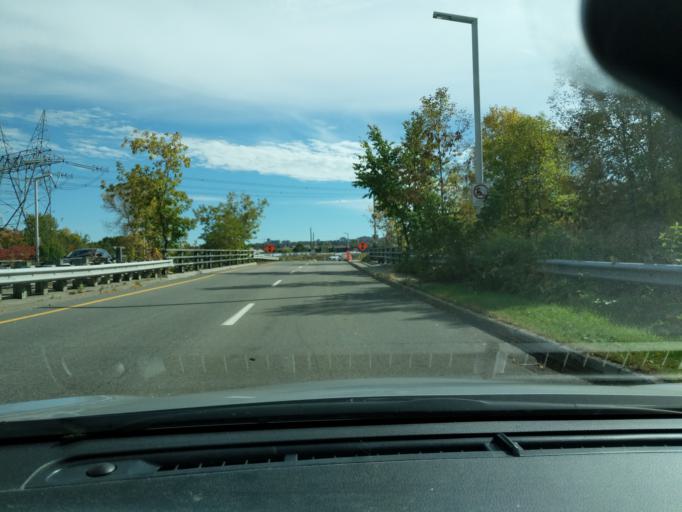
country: CA
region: Quebec
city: L'Ancienne-Lorette
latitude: 46.8023
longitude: -71.3241
